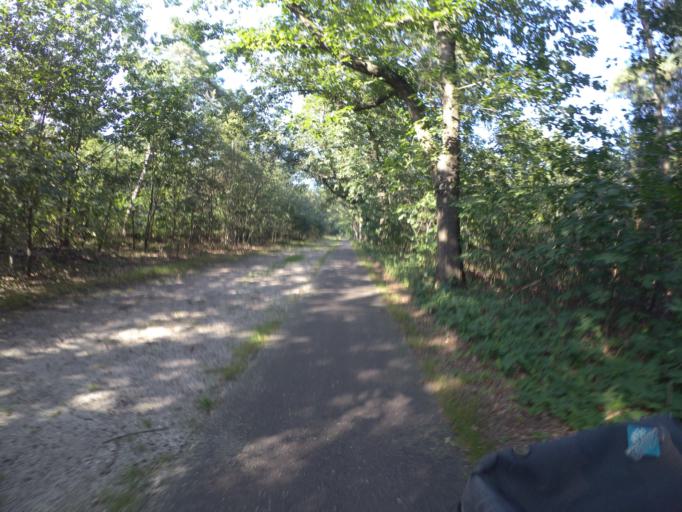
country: NL
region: North Brabant
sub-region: Gemeente Landerd
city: Schaijk
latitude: 51.7197
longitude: 5.6292
